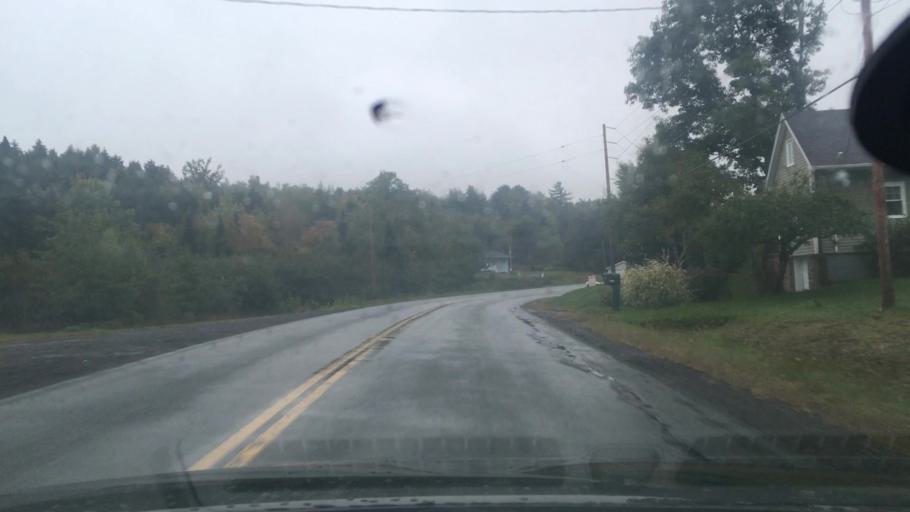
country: CA
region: Nova Scotia
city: Windsor
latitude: 44.8344
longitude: -64.2548
